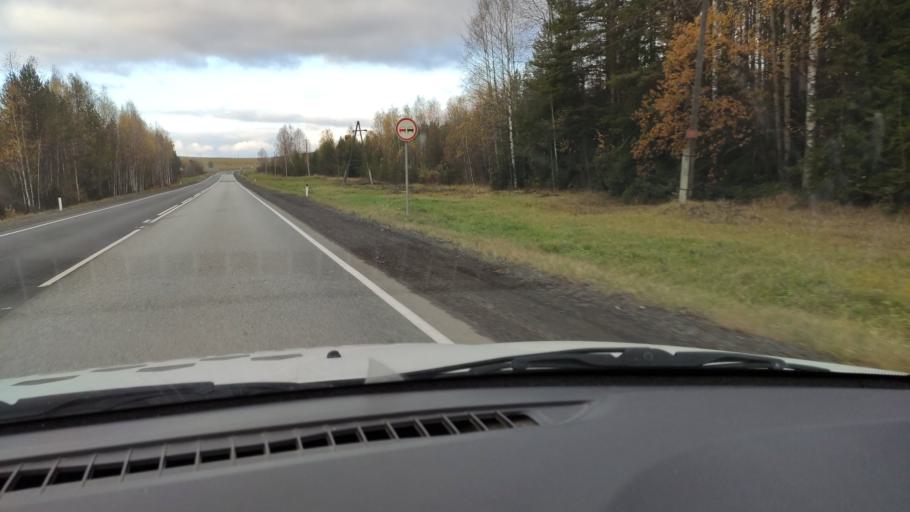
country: RU
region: Kirov
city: Belaya Kholunitsa
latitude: 58.8867
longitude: 50.8743
